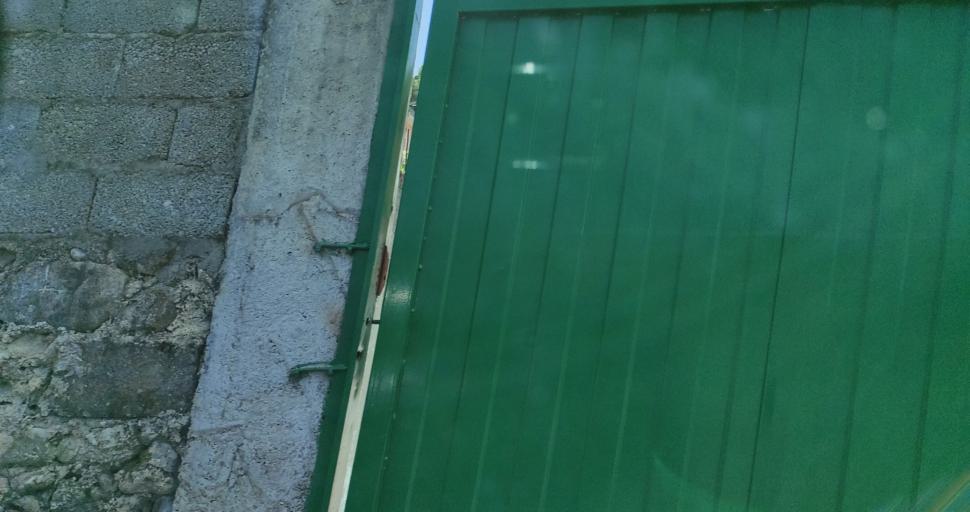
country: AL
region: Shkoder
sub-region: Rrethi i Malesia e Madhe
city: Gruemire
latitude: 42.1239
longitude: 19.5885
